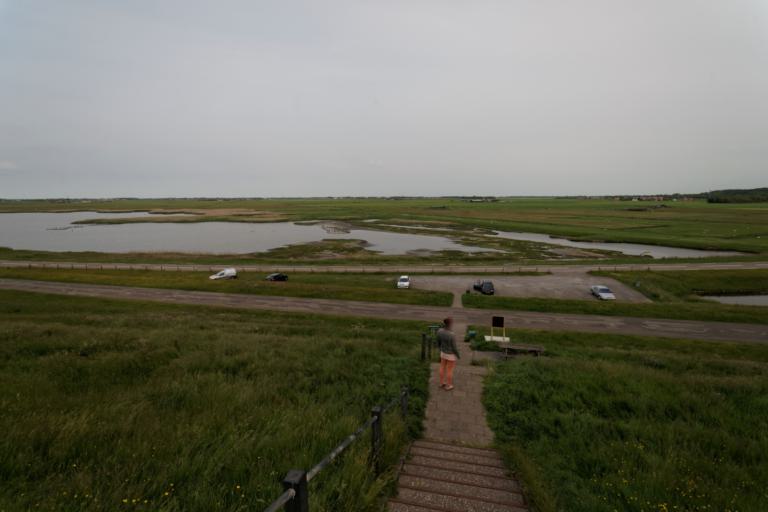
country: NL
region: North Holland
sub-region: Gemeente Bergen
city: Egmond aan Zee
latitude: 52.7338
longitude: 4.6428
